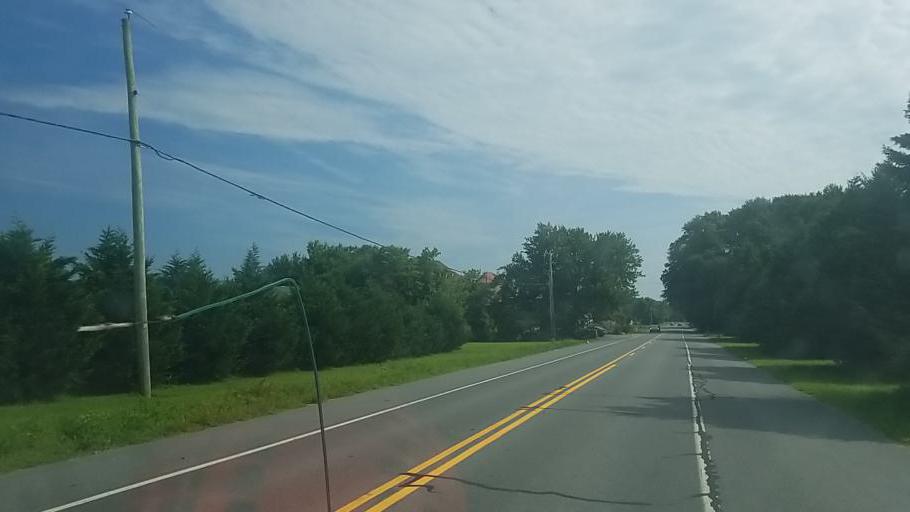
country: US
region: Delaware
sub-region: Sussex County
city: Selbyville
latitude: 38.5372
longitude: -75.1852
